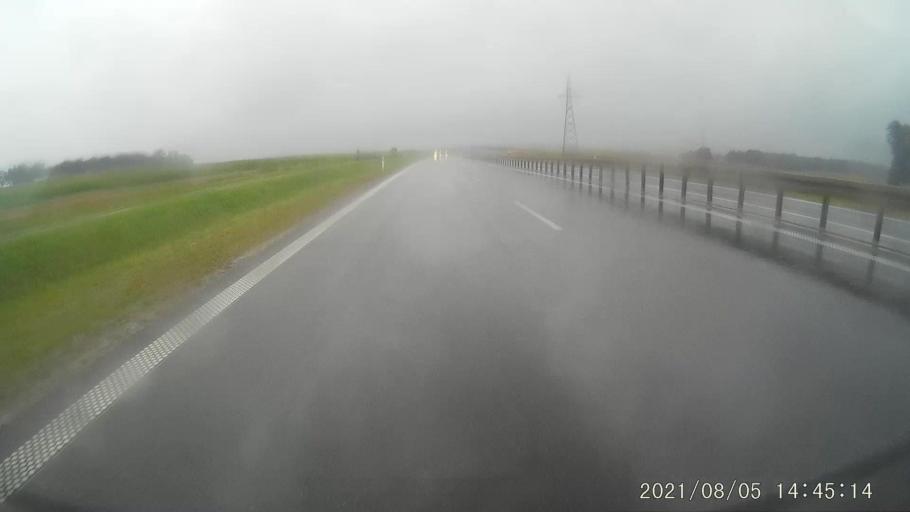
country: PL
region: Opole Voivodeship
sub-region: Powiat nyski
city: Nysa
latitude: 50.4984
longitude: 17.3632
